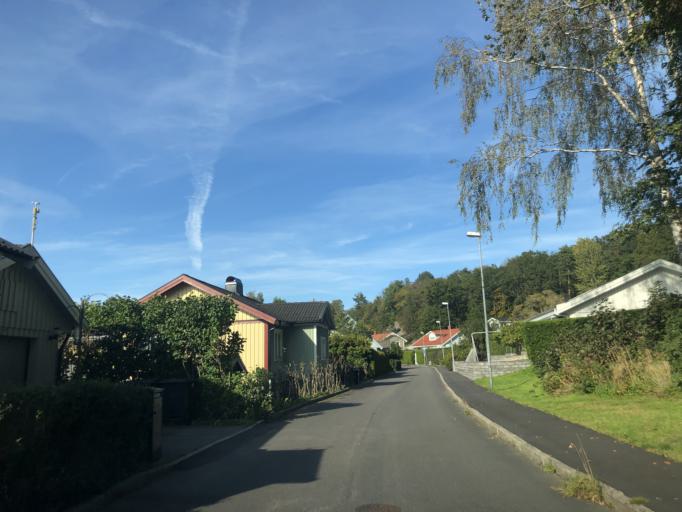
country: SE
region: Vaestra Goetaland
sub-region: Molndal
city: Moelndal
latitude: 57.6605
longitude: 12.0288
